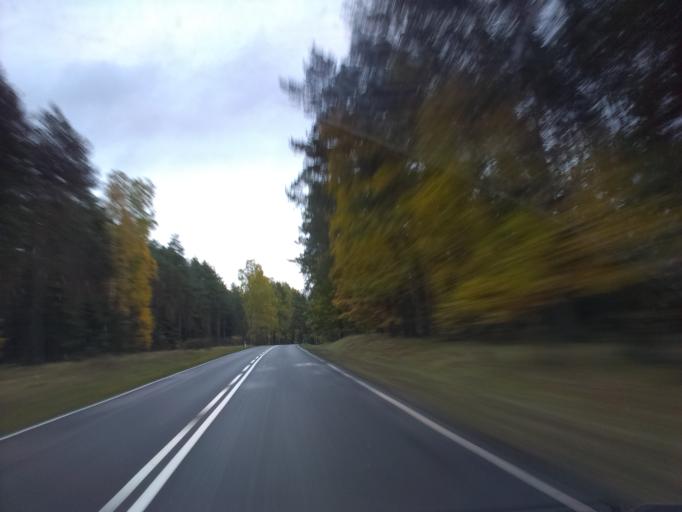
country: PL
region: Kujawsko-Pomorskie
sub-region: Powiat tucholski
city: Tuchola
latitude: 53.5518
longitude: 17.9209
